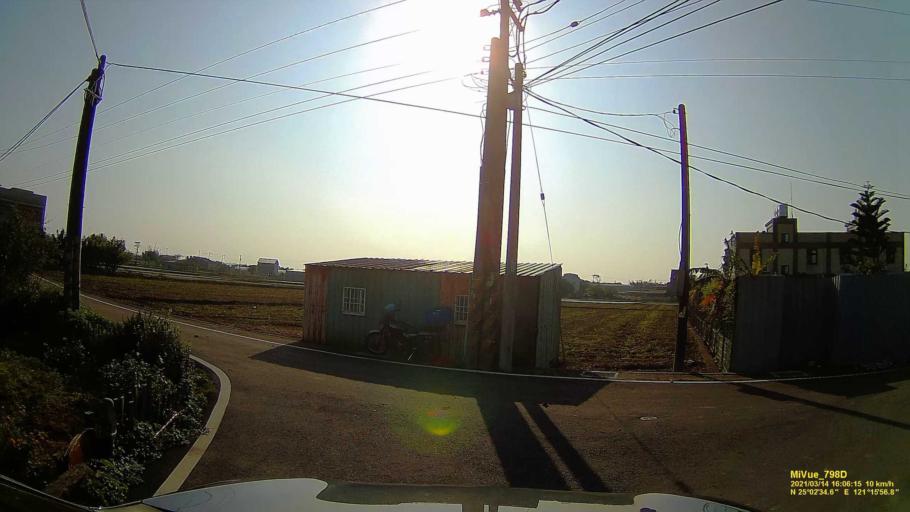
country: TW
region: Taiwan
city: Taoyuan City
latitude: 25.0429
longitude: 121.2658
